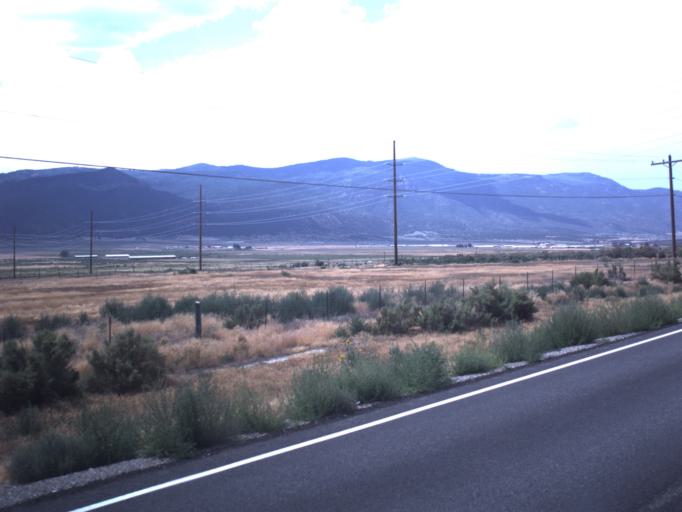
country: US
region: Utah
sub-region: Sanpete County
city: Moroni
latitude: 39.5479
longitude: -111.5984
